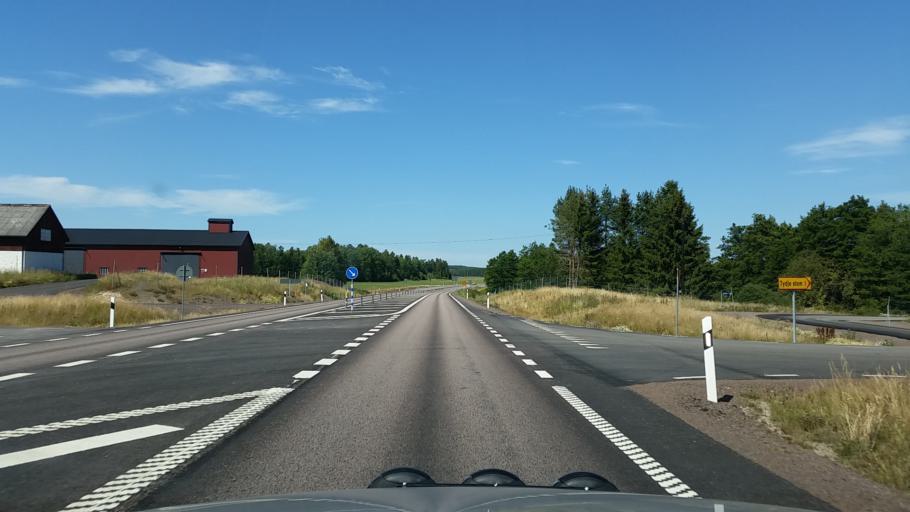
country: SE
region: Vaestra Goetaland
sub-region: Amals Kommun
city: Amal
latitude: 58.9553
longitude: 12.6077
